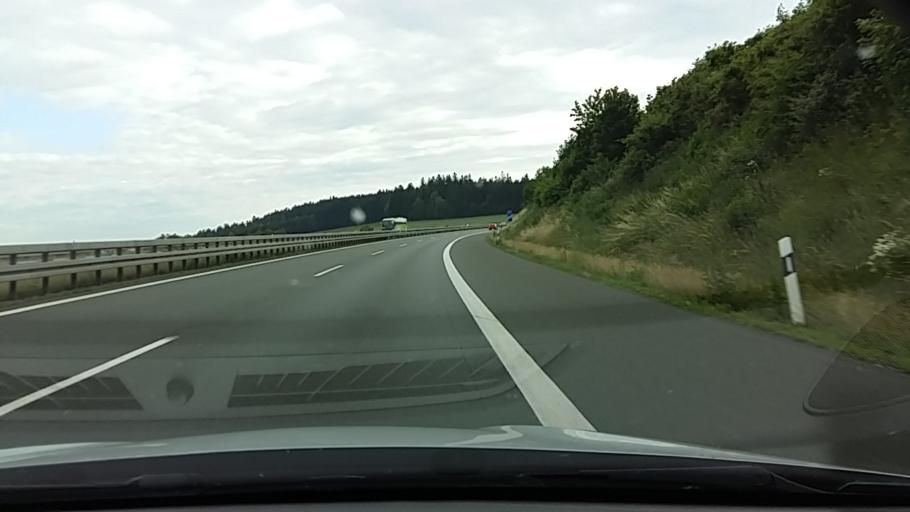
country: DE
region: Bavaria
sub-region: Upper Palatinate
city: Leuchtenberg
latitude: 49.5788
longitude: 12.2759
